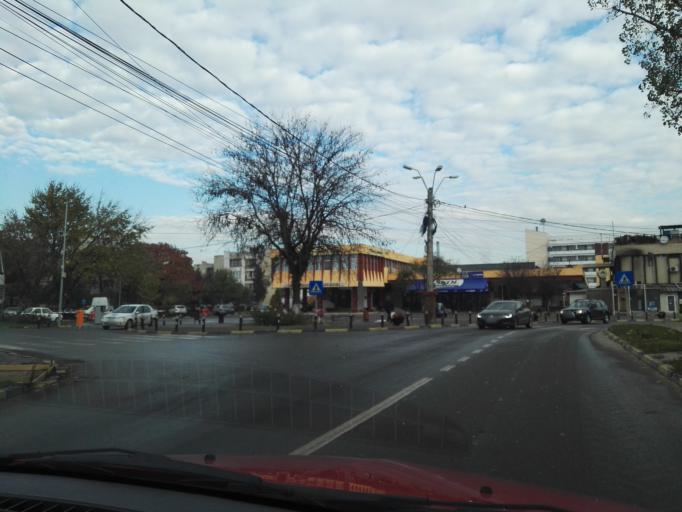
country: RO
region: Ilfov
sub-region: Comuna Magurele
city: Magurele
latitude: 44.3495
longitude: 26.0298
